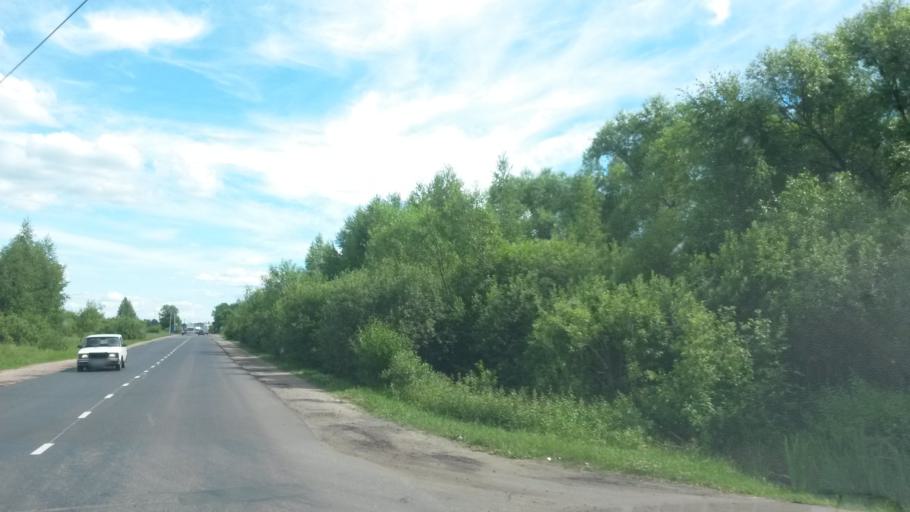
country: RU
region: Ivanovo
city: Zavolzhsk
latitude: 57.5005
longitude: 42.1186
